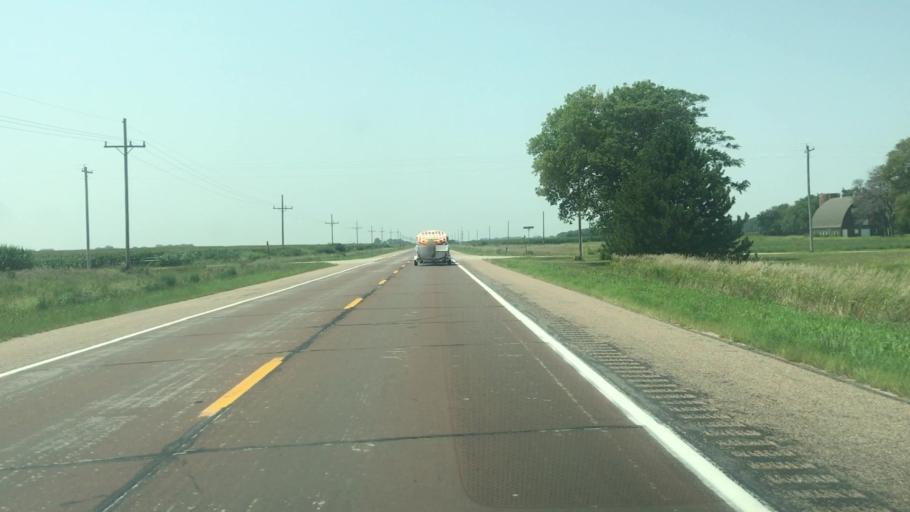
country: US
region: Nebraska
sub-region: Hall County
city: Grand Island
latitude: 40.9674
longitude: -98.4544
